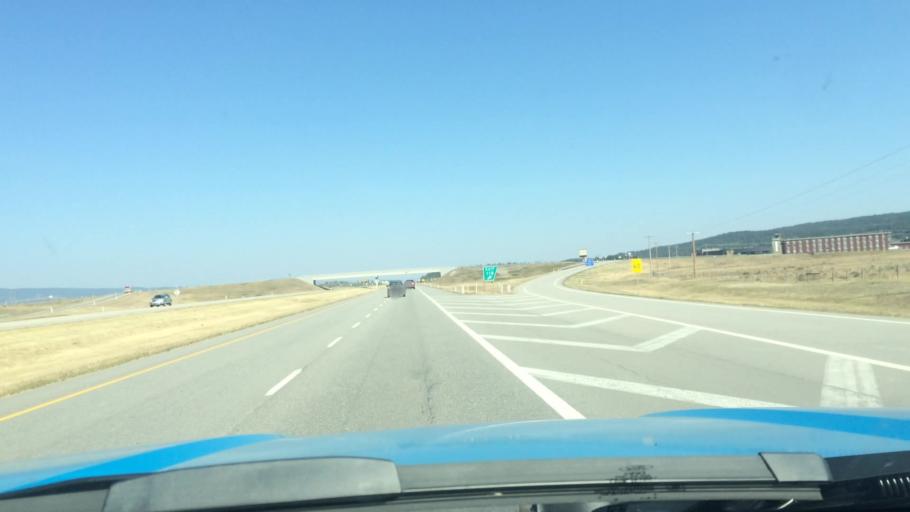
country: CA
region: Alberta
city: Canmore
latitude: 51.1015
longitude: -115.0259
